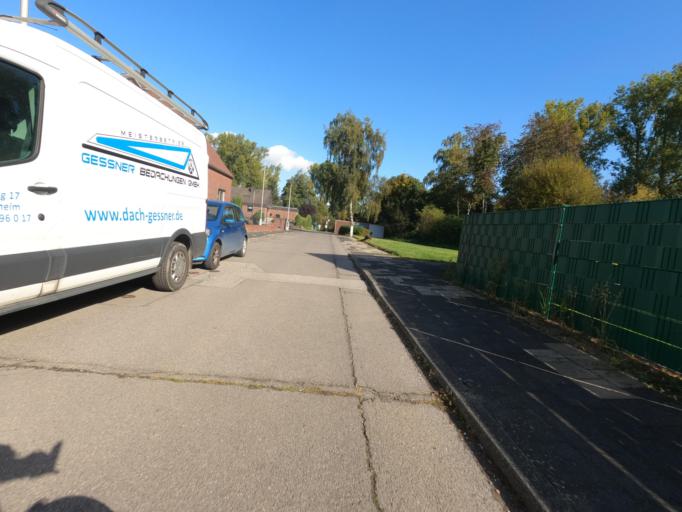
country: DE
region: North Rhine-Westphalia
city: Julich
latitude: 50.8979
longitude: 6.3600
